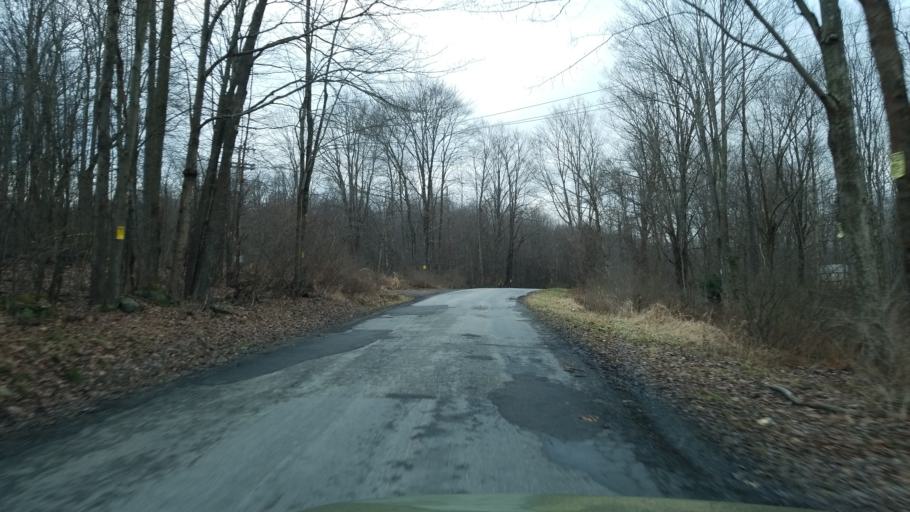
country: US
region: Pennsylvania
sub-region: Jefferson County
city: Falls Creek
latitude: 41.1738
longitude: -78.7905
